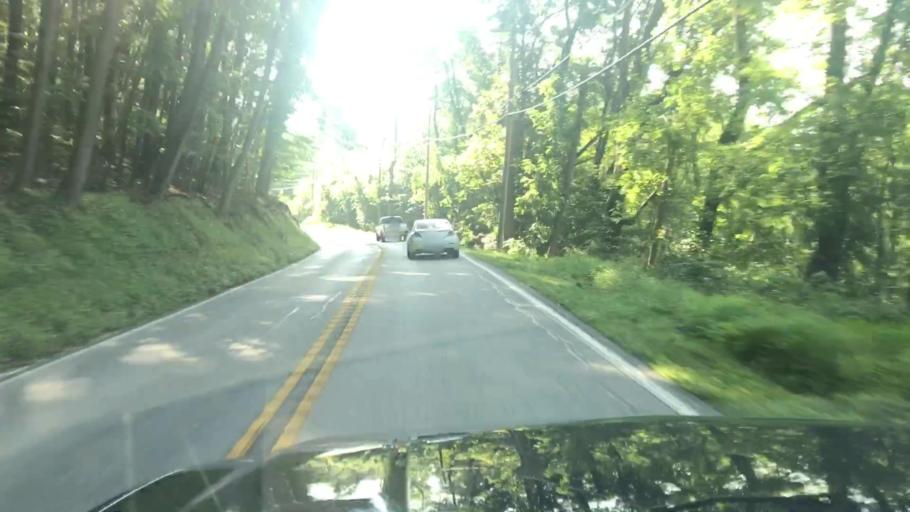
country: US
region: Pennsylvania
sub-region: York County
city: Valley Green
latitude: 40.1510
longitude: -76.8241
